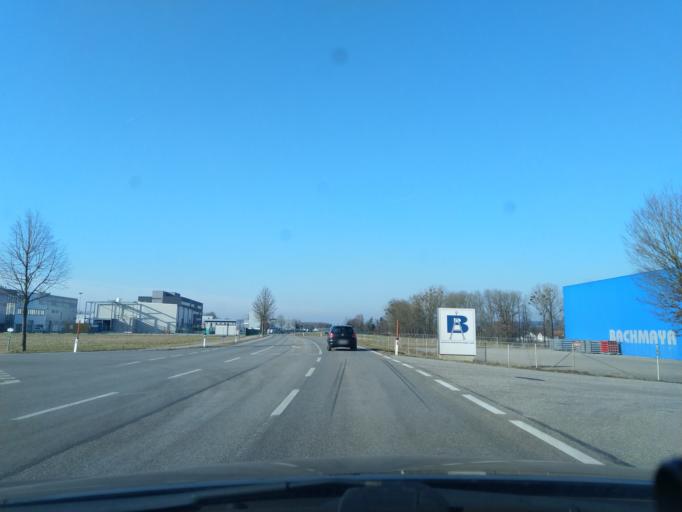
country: AT
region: Upper Austria
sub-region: Politischer Bezirk Scharding
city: Sankt Marienkirchen bei Schaerding
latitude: 48.3017
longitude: 13.4305
